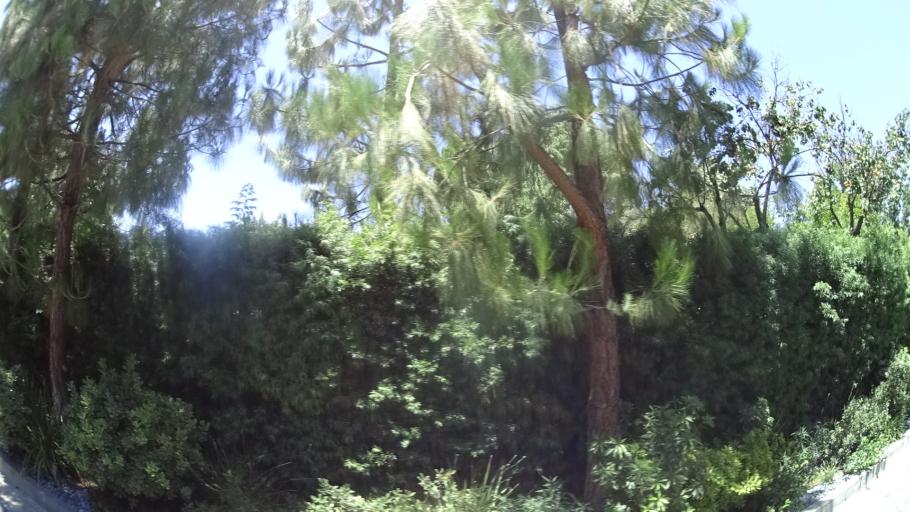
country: US
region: California
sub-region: Los Angeles County
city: Sherman Oaks
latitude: 34.1491
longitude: -118.4757
